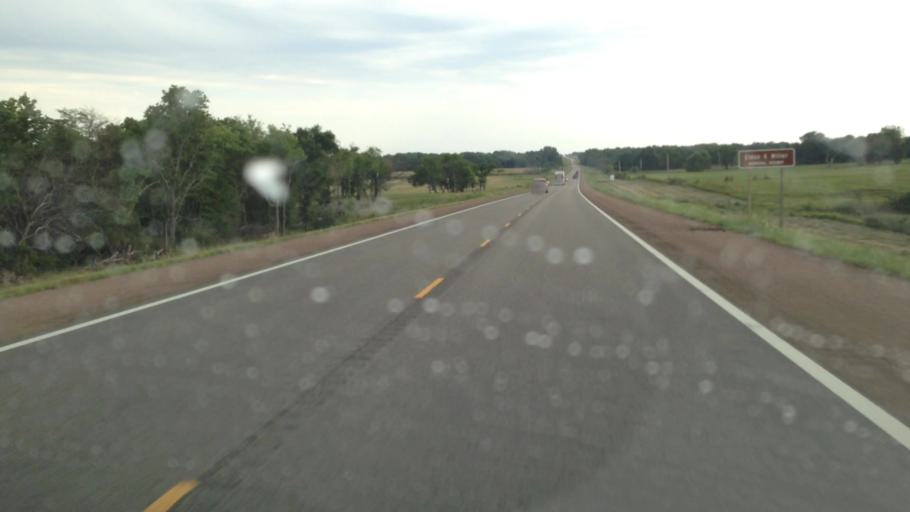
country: US
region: Kansas
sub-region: Coffey County
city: Burlington
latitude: 38.0387
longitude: -95.7391
